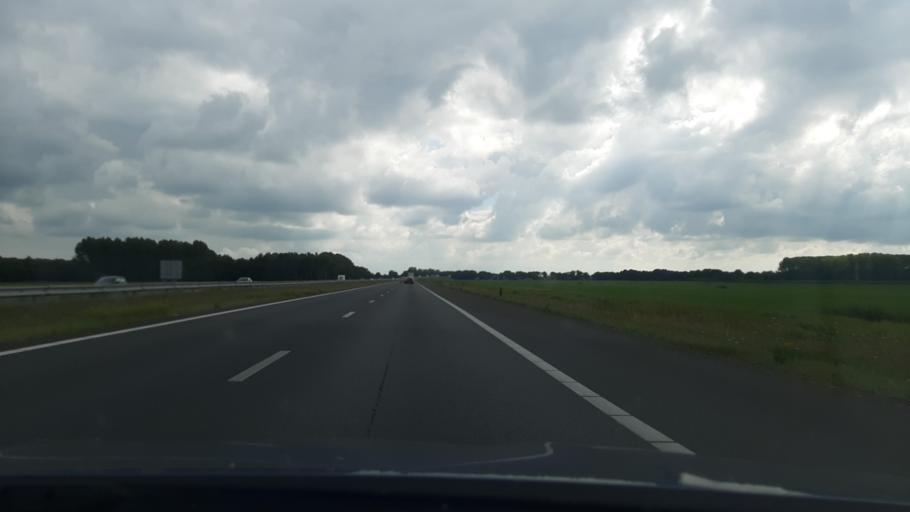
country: NL
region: Friesland
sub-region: Gemeente Opsterland
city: Tijnje
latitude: 53.0064
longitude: 5.9974
